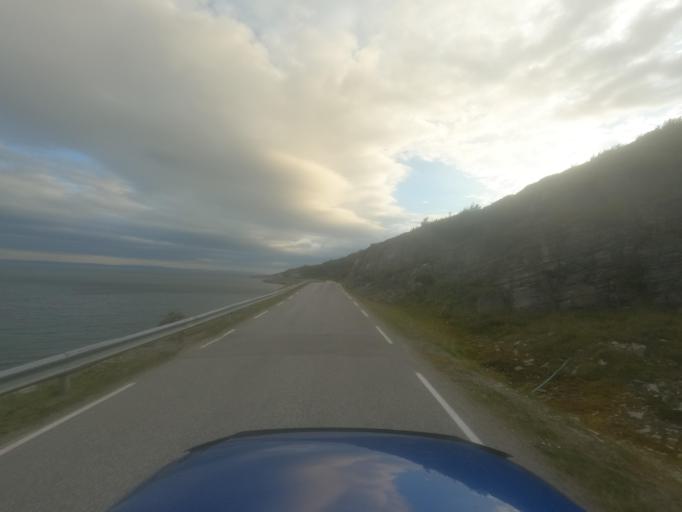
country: NO
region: Finnmark Fylke
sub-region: Nordkapp
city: Honningsvag
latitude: 70.7041
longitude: 25.5194
